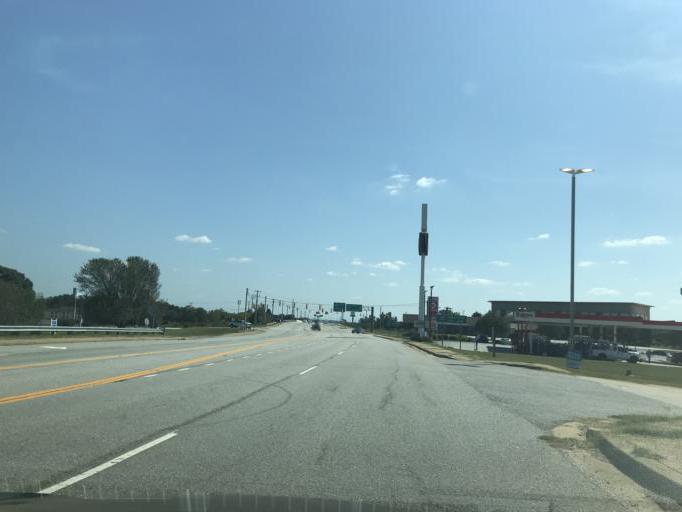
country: US
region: South Carolina
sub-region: Cherokee County
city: Gaffney
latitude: 35.0854
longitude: -81.7084
